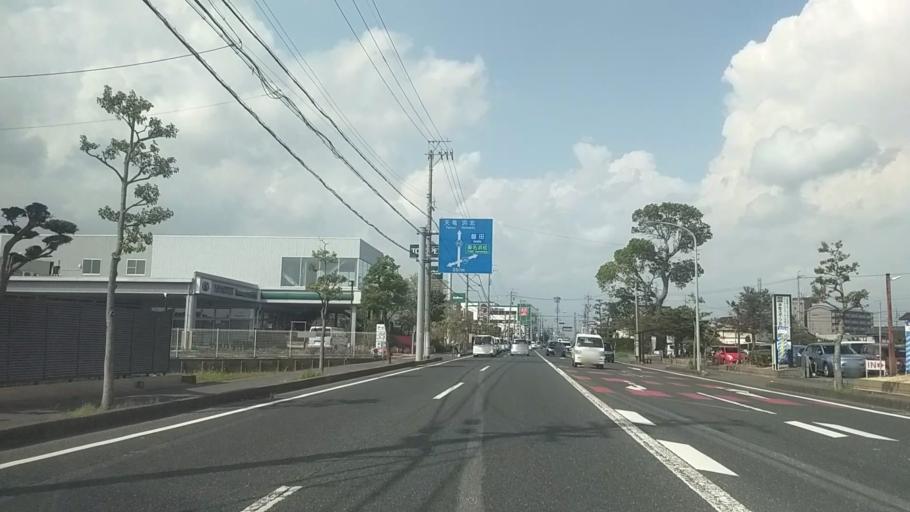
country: JP
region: Shizuoka
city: Hamamatsu
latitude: 34.7174
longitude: 137.7625
